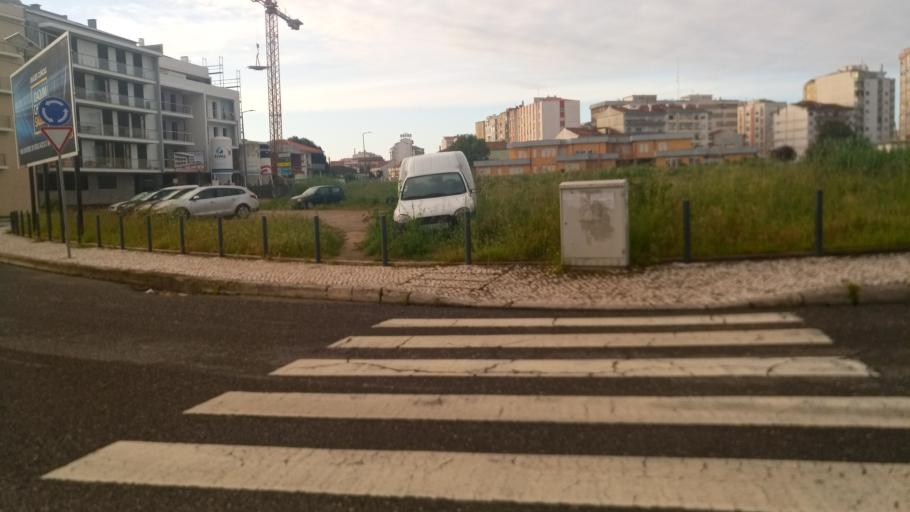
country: PT
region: Leiria
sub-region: Caldas da Rainha
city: Caldas da Rainha
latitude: 39.4129
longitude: -9.1396
